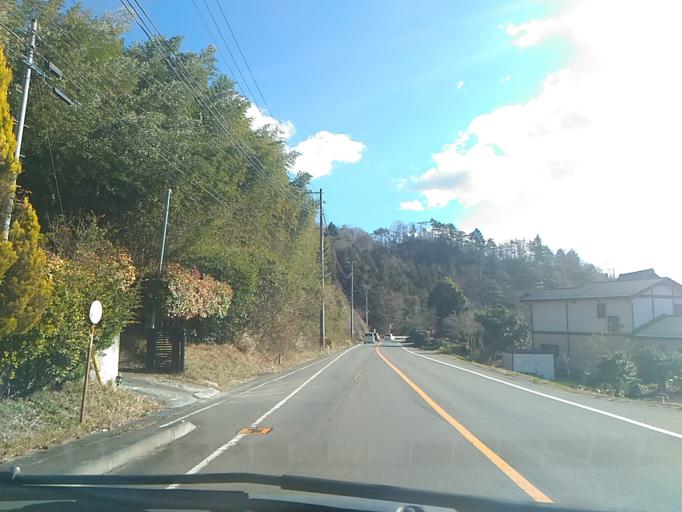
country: JP
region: Fukushima
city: Iwaki
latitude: 37.0120
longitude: 140.7752
